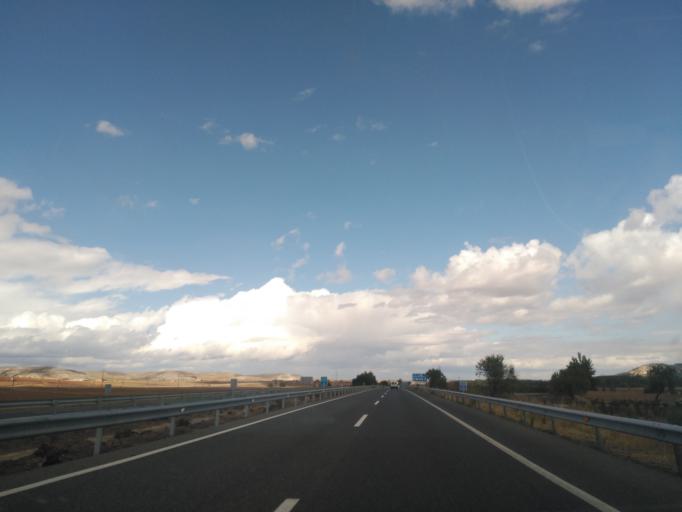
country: ES
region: Castille and Leon
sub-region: Provincia de Burgos
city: Villaquiran de los Infantes
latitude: 42.2281
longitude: -3.9936
